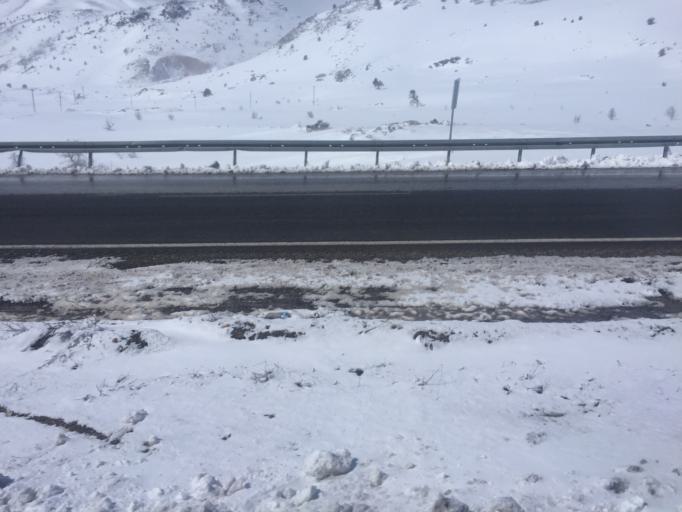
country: TR
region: Kahramanmaras
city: Goksun
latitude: 38.1842
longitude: 36.4564
